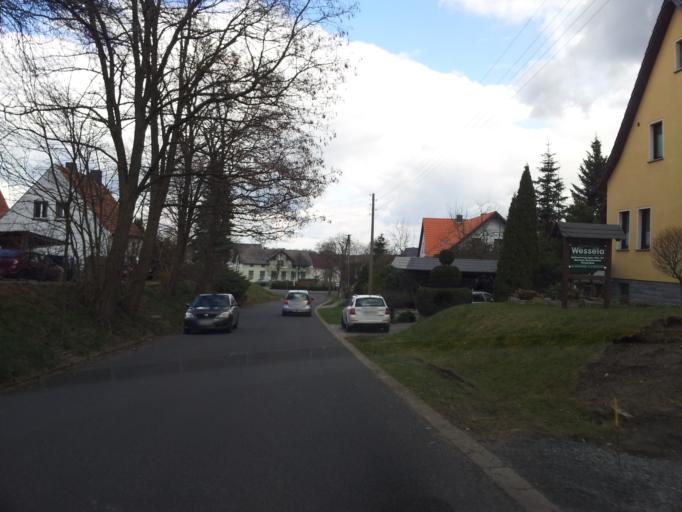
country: DE
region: Saxony
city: Rackelwitz
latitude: 51.2848
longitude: 14.2260
